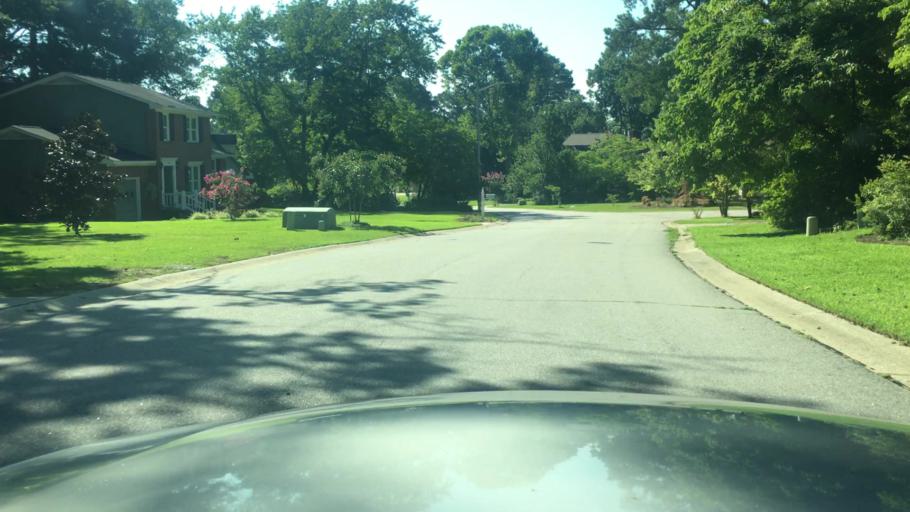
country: US
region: North Carolina
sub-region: Cumberland County
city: Fayetteville
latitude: 35.1138
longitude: -78.9020
